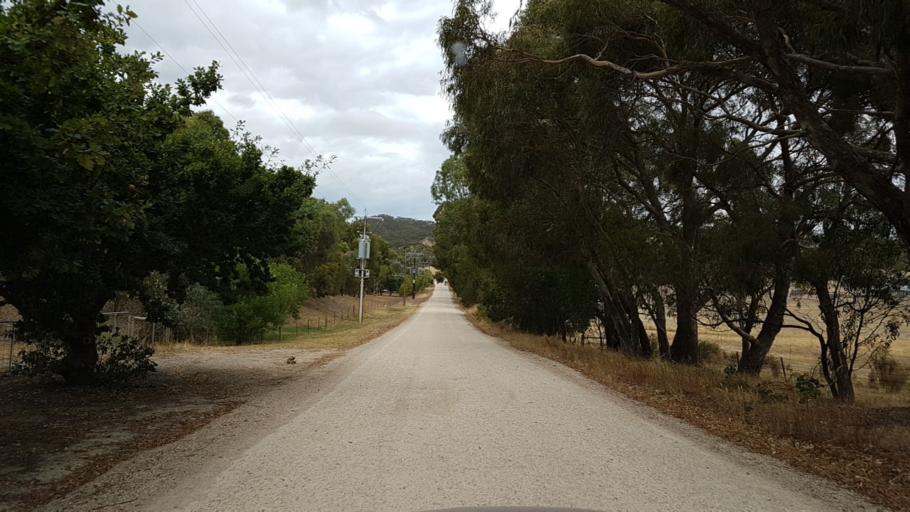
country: AU
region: South Australia
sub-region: Adelaide Hills
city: Gumeracha
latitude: -34.7826
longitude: 138.8588
